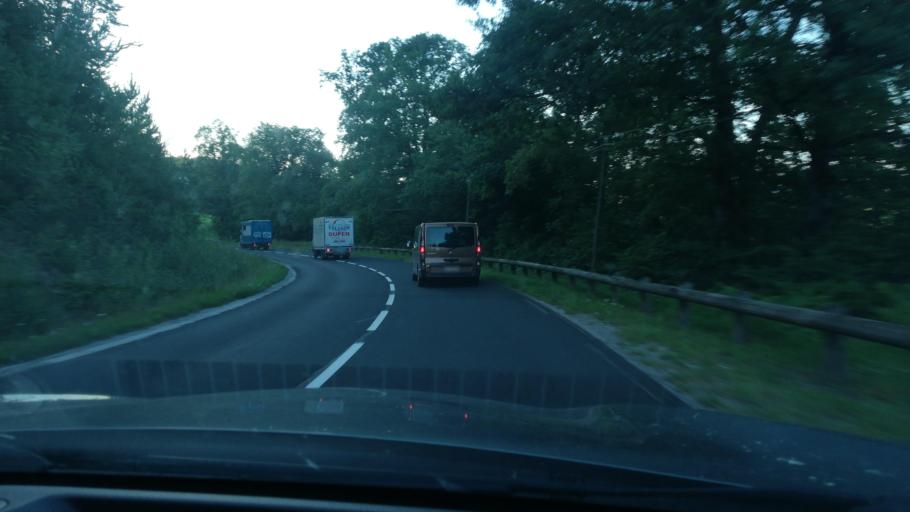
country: FR
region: Auvergne
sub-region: Departement du Cantal
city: Laroquebrou
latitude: 44.9303
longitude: 2.0778
